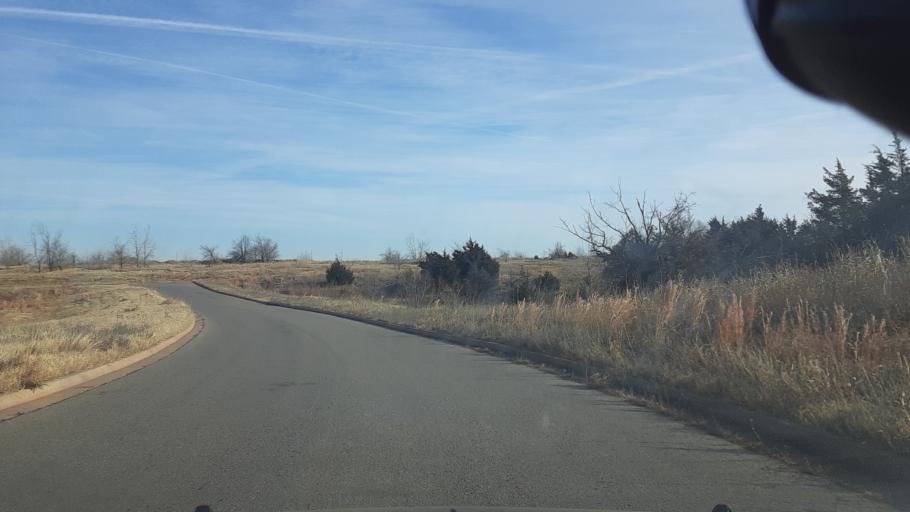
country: US
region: Oklahoma
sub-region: Logan County
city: Guthrie
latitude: 35.8589
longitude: -97.4238
